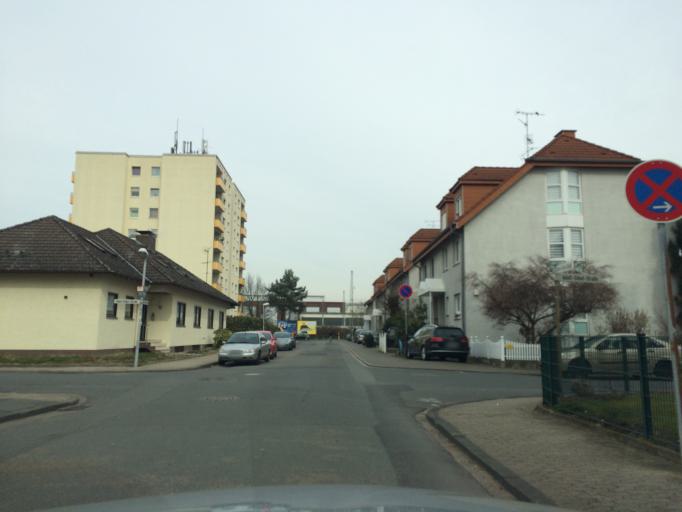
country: DE
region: Hesse
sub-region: Regierungsbezirk Darmstadt
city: Gross-Gerau
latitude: 49.9231
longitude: 8.4872
